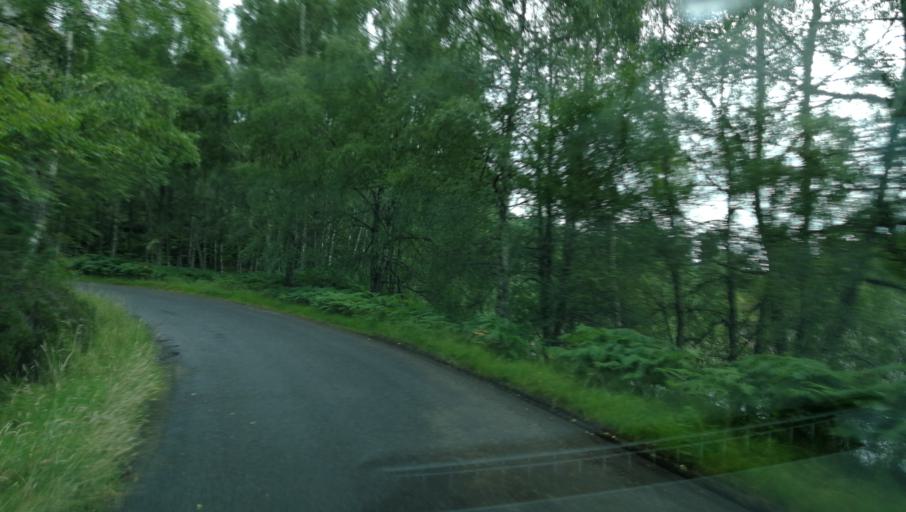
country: GB
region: Scotland
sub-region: Highland
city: Spean Bridge
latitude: 57.3037
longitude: -4.8740
